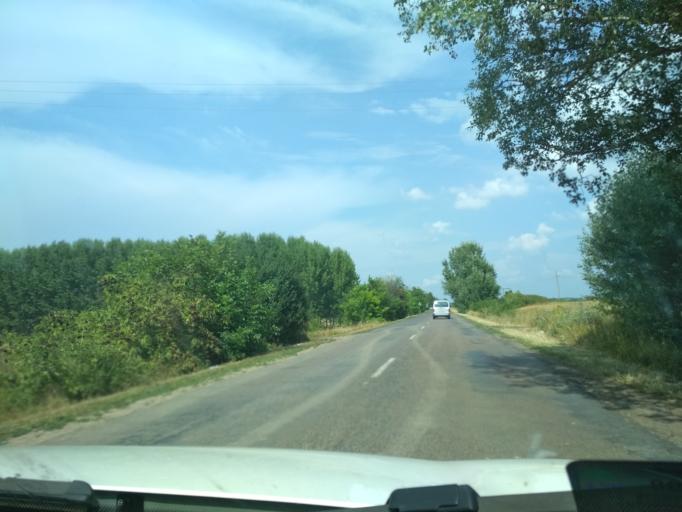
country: HU
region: Jasz-Nagykun-Szolnok
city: Abadszalok
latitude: 47.4946
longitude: 20.6234
